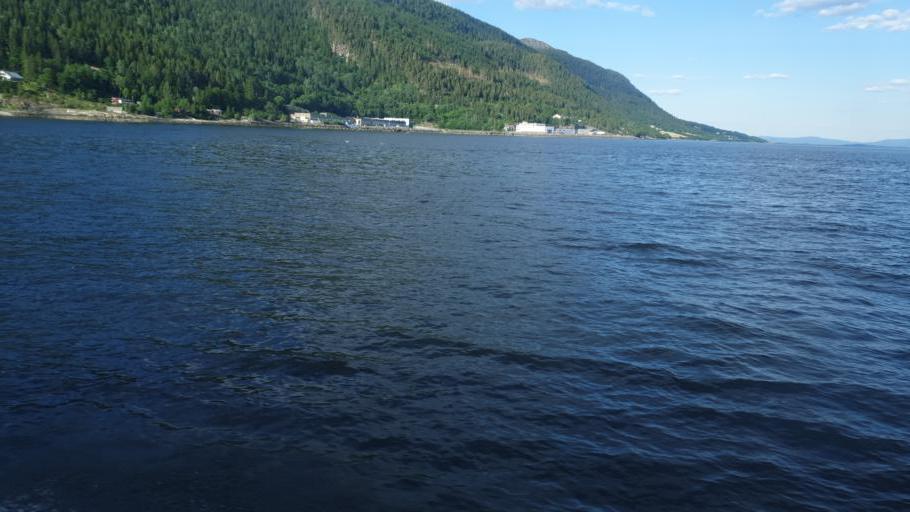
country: NO
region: Sor-Trondelag
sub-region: Trondheim
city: Trondheim
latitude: 63.5519
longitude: 10.2270
